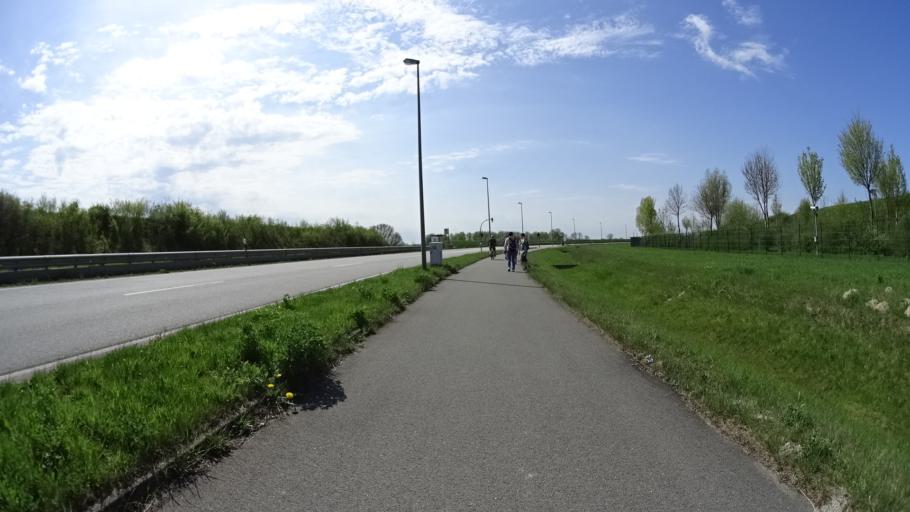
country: DE
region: Lower Saxony
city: Neu Wulmstorf
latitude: 53.5301
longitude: 9.8428
